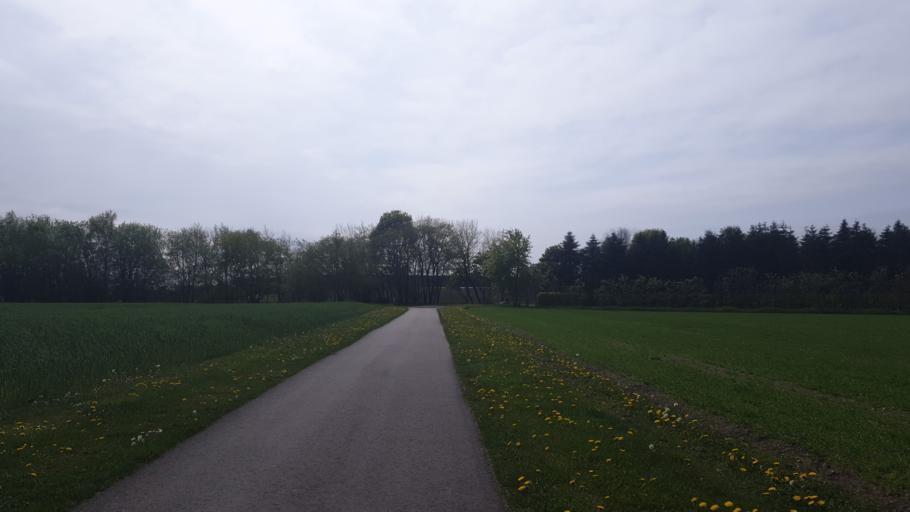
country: DK
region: Central Jutland
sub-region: Hedensted Kommune
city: Hedensted
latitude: 55.7915
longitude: 9.6883
